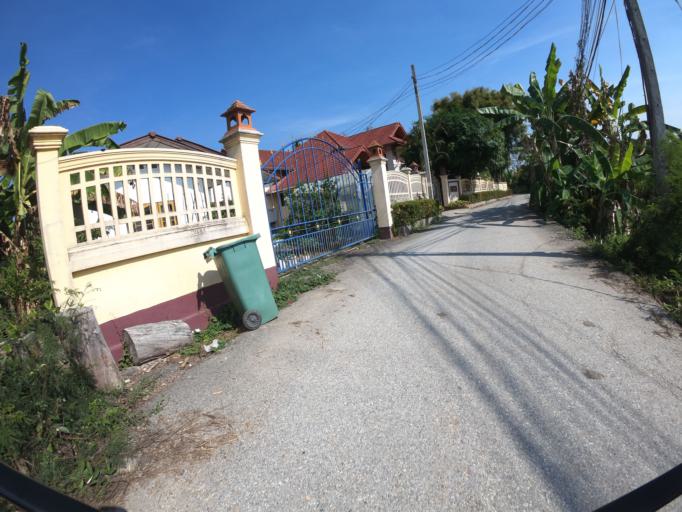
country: TH
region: Chiang Mai
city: San Sai
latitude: 18.8509
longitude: 98.9985
